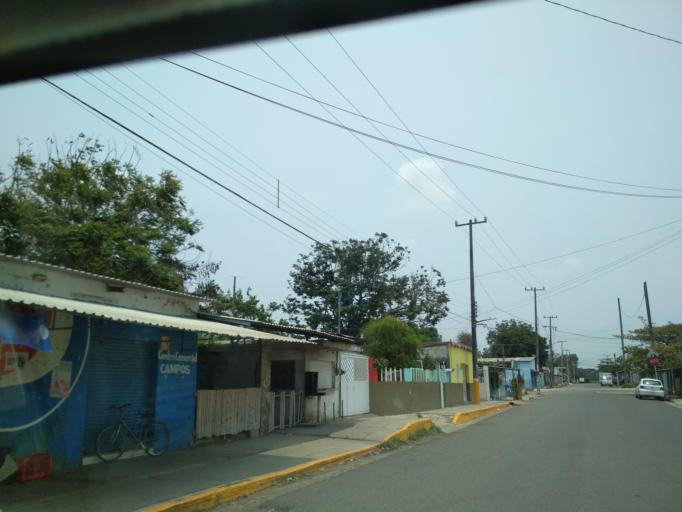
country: MX
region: Veracruz
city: Manlio Fabio Altamirano
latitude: 19.1313
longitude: -96.2965
